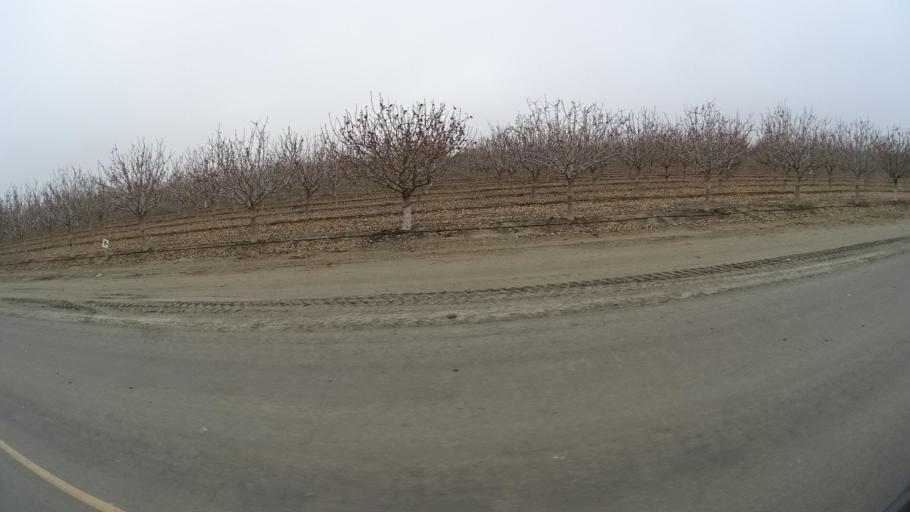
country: US
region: California
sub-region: Kern County
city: Rosedale
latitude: 35.2043
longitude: -119.2329
